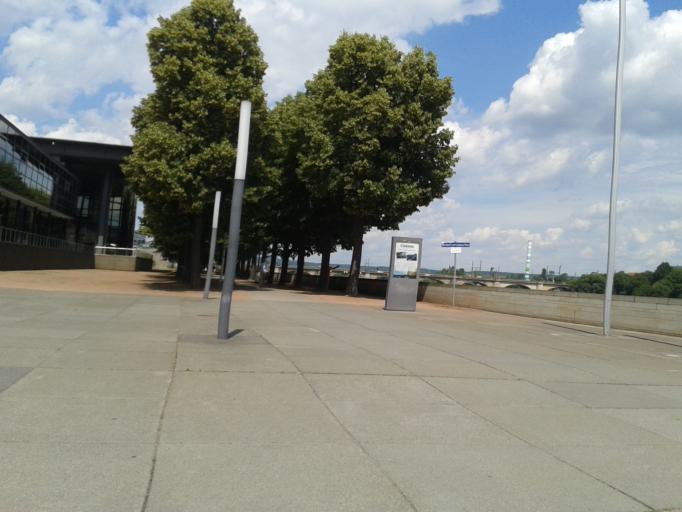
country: DE
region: Saxony
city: Dresden
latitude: 51.0565
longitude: 13.7344
